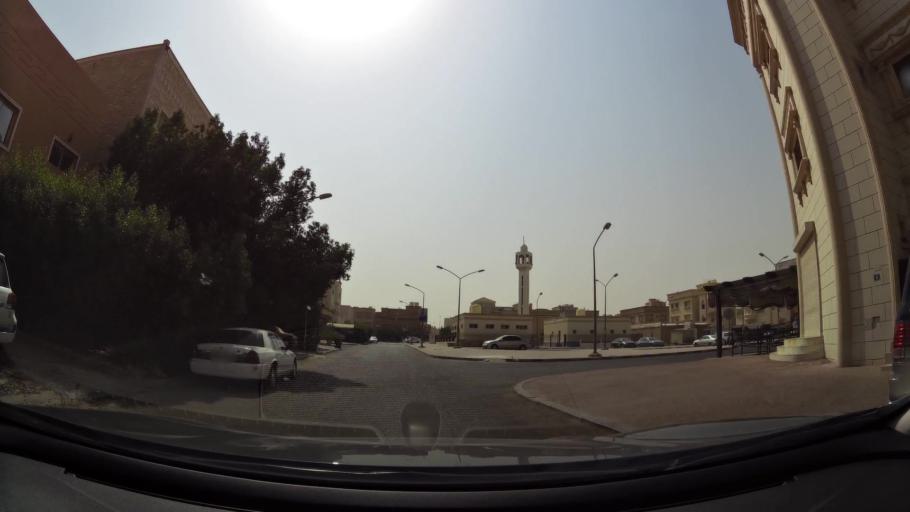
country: KW
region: Muhafazat al Jahra'
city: Al Jahra'
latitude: 29.3047
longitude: 47.7166
